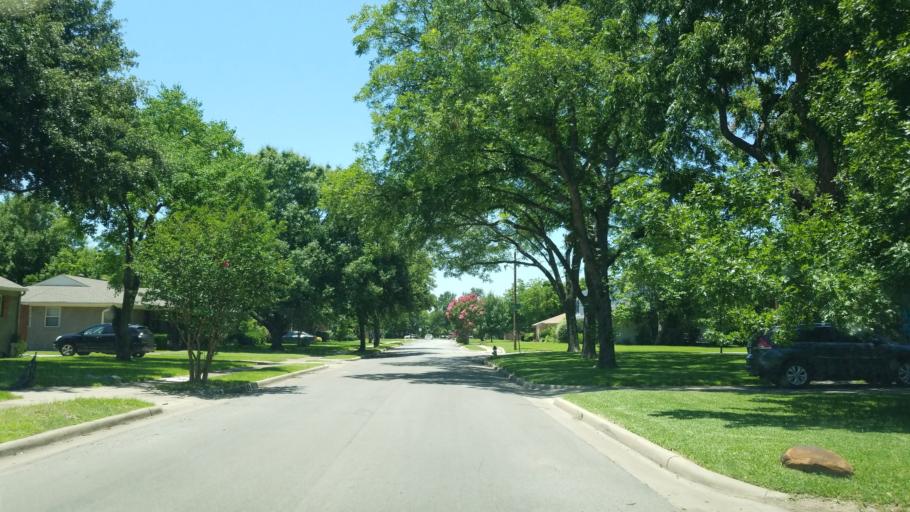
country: US
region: Texas
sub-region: Dallas County
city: University Park
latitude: 32.8715
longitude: -96.8511
